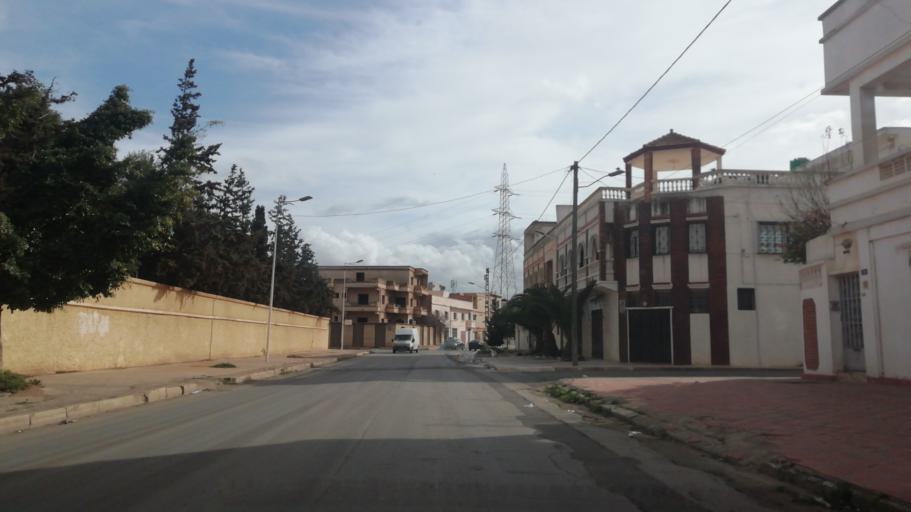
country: DZ
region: Oran
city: Es Senia
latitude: 35.6627
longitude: -0.6387
